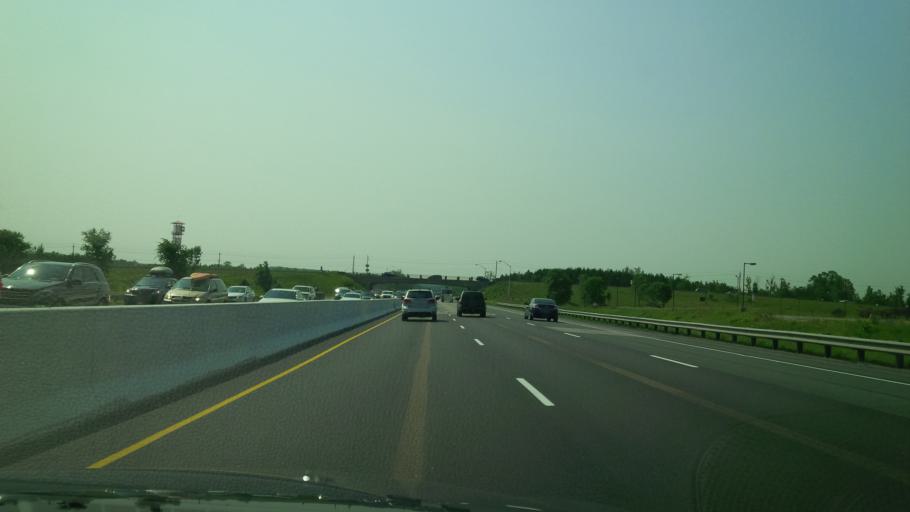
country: CA
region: Ontario
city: Bradford West Gwillimbury
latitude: 44.2026
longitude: -79.6561
